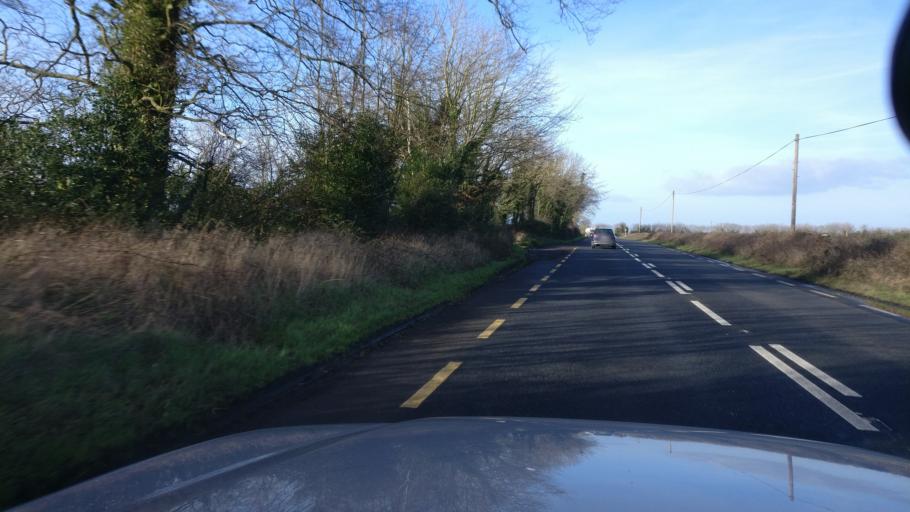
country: IE
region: Leinster
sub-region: Uibh Fhaili
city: Tullamore
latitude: 53.2033
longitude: -7.4333
